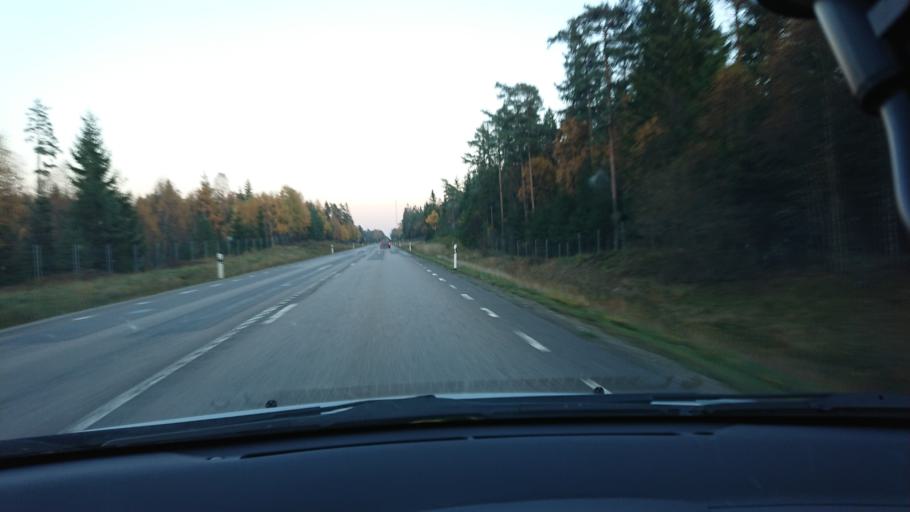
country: SE
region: Halland
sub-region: Laholms Kommun
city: Knared
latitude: 56.7341
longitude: 13.4167
